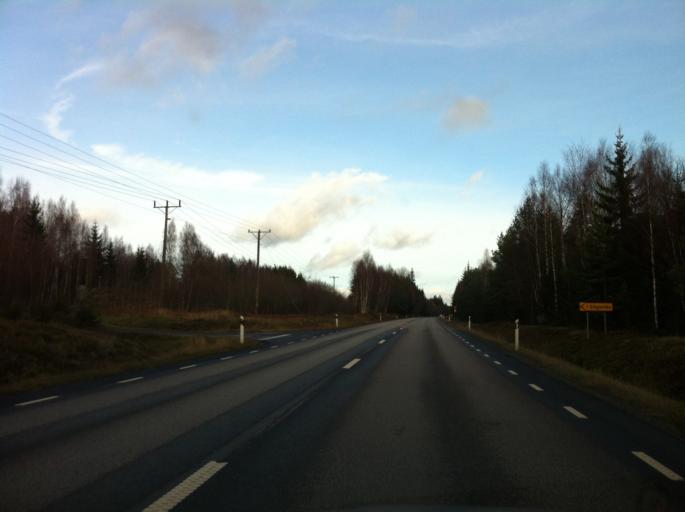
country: SE
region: Kronoberg
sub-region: Almhults Kommun
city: AElmhult
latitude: 56.5796
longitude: 14.1891
